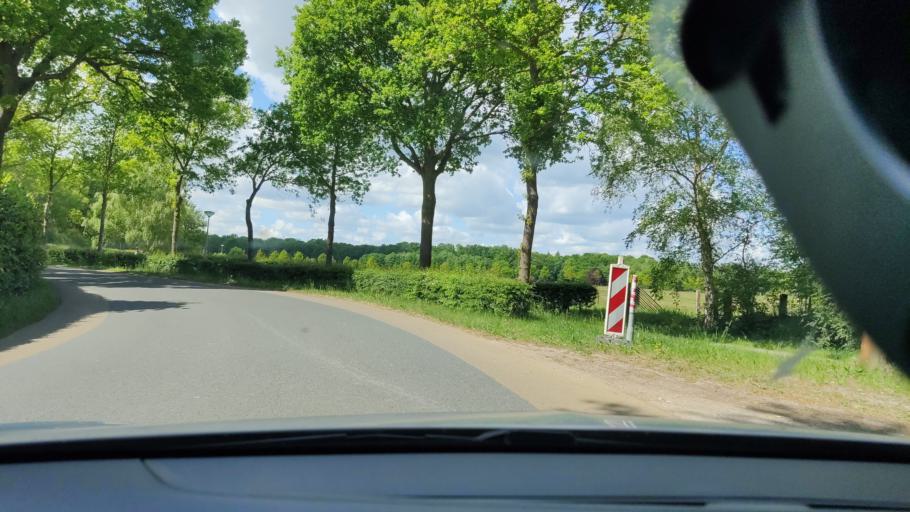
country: NL
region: Drenthe
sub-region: Gemeente Tynaarlo
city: Zuidlaren
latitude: 53.1082
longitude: 6.6834
